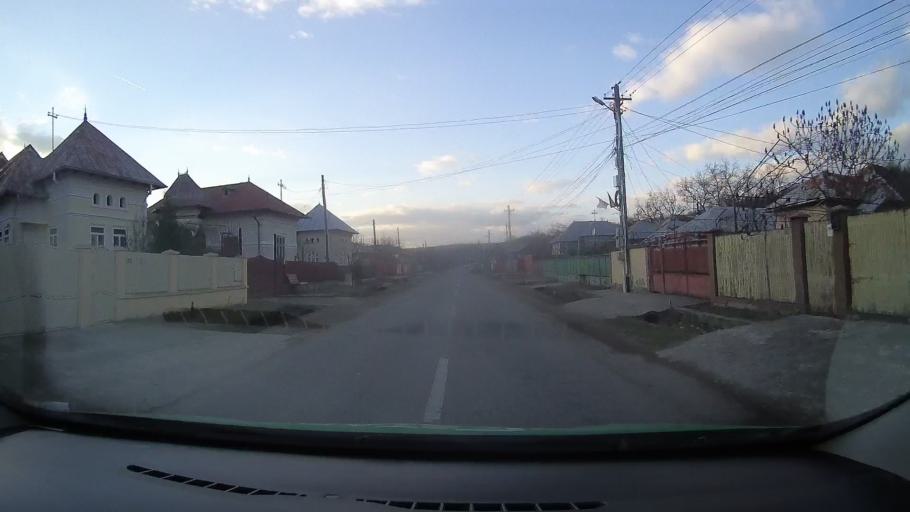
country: RO
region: Dambovita
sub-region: Comuna Gura Ocnitei
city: Adanca
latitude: 44.9305
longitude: 25.6012
